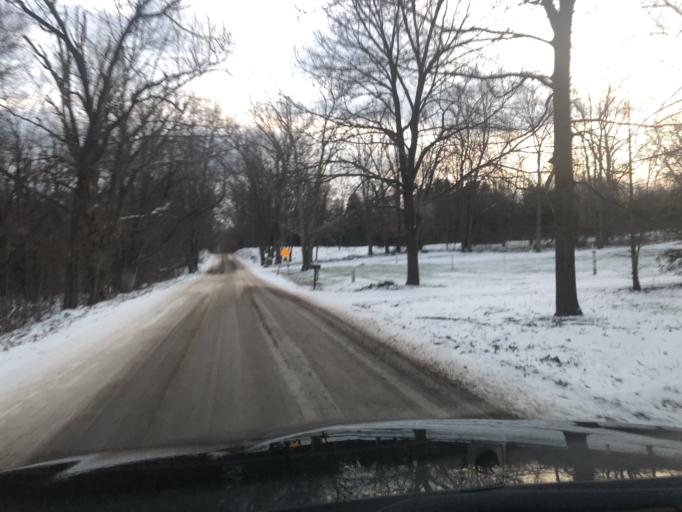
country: US
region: Michigan
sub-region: Oakland County
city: Milford
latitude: 42.5759
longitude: -83.6393
